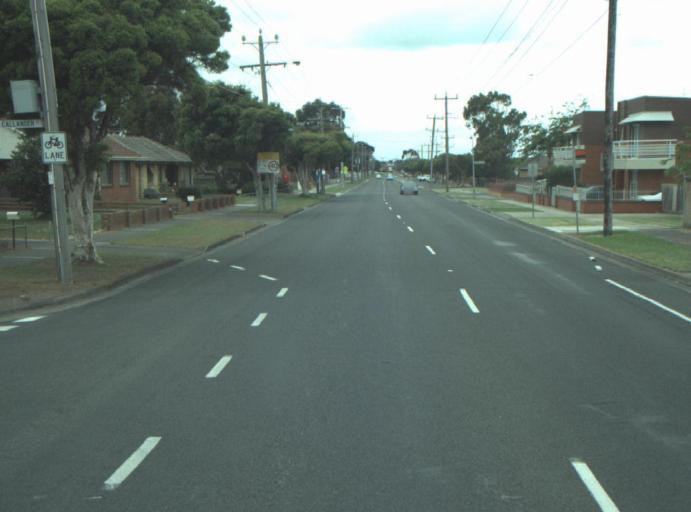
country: AU
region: Victoria
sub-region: Greater Geelong
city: Breakwater
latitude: -38.1735
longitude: 144.3786
